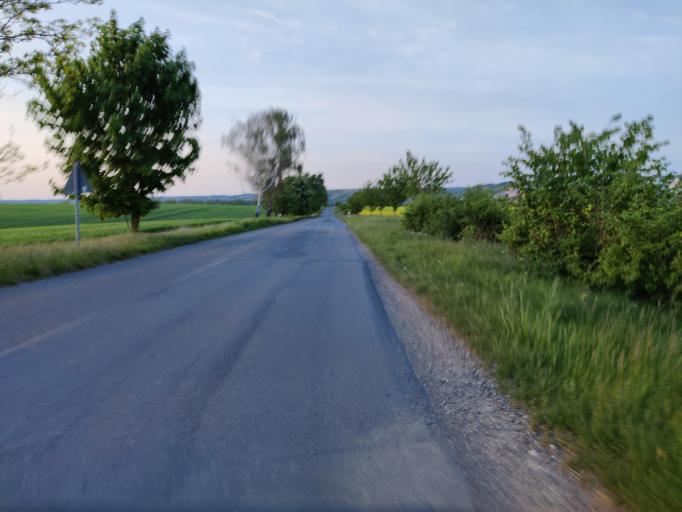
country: DE
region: Saxony-Anhalt
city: Karsdorf
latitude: 51.2588
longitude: 11.6440
